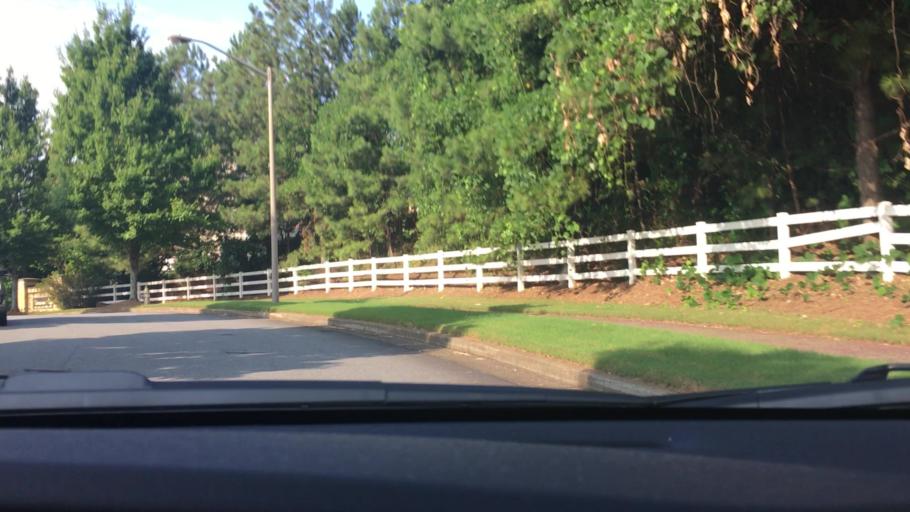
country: US
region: Georgia
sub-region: Cobb County
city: Marietta
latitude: 34.0009
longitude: -84.5667
